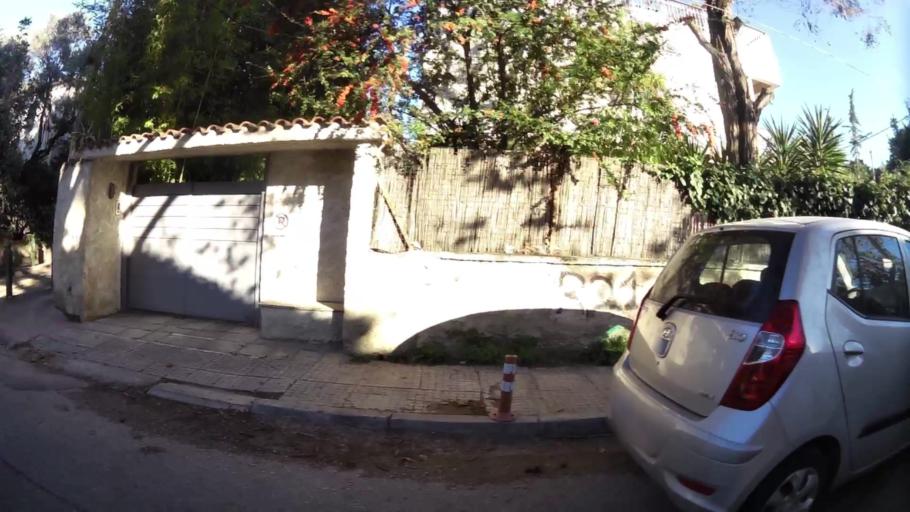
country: GR
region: Attica
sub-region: Nomarchia Athinas
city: Kifisia
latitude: 38.0747
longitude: 23.8042
